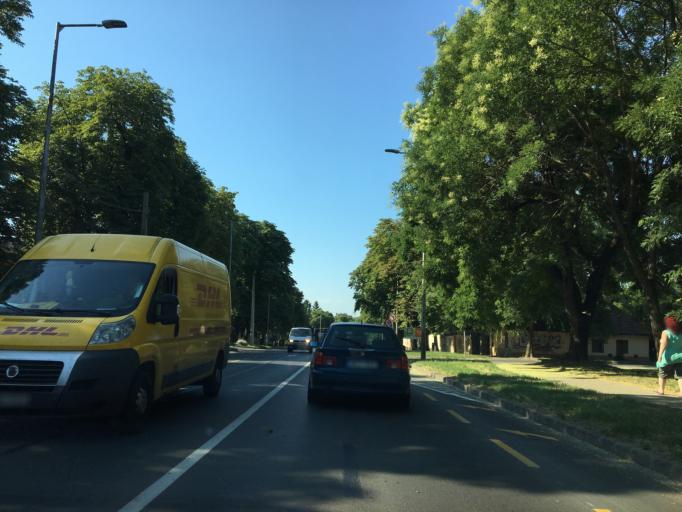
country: HU
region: Tolna
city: Szekszard
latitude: 46.3576
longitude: 18.7040
